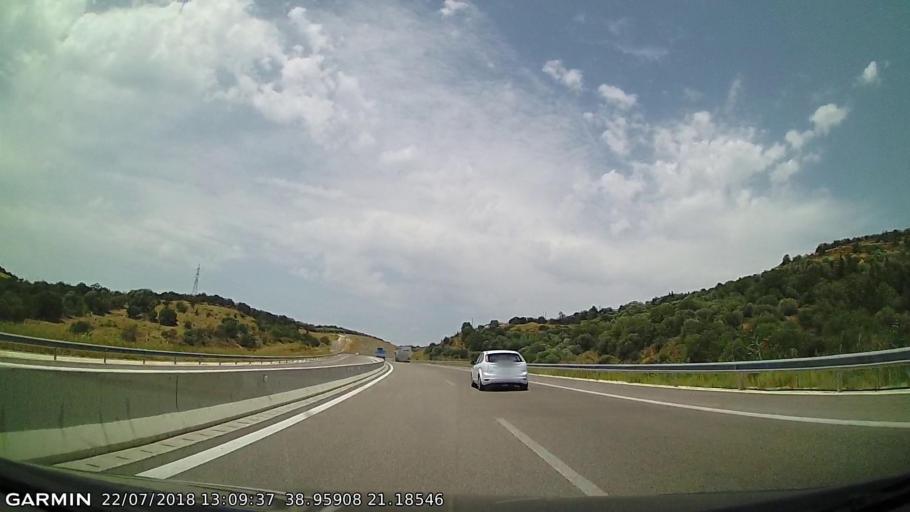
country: GR
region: West Greece
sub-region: Nomos Aitolias kai Akarnanias
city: Krikellos
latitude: 38.9591
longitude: 21.1854
